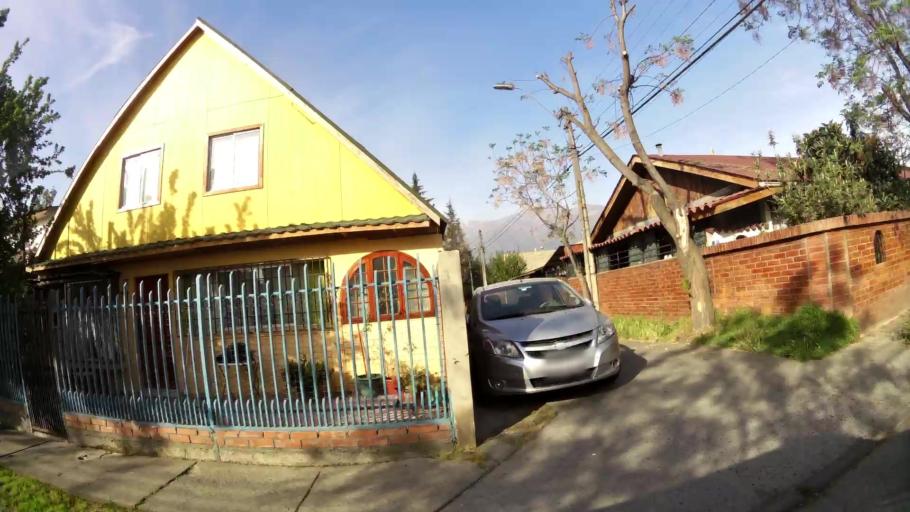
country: CL
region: Santiago Metropolitan
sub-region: Provincia de Santiago
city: La Pintana
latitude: -33.5422
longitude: -70.5845
